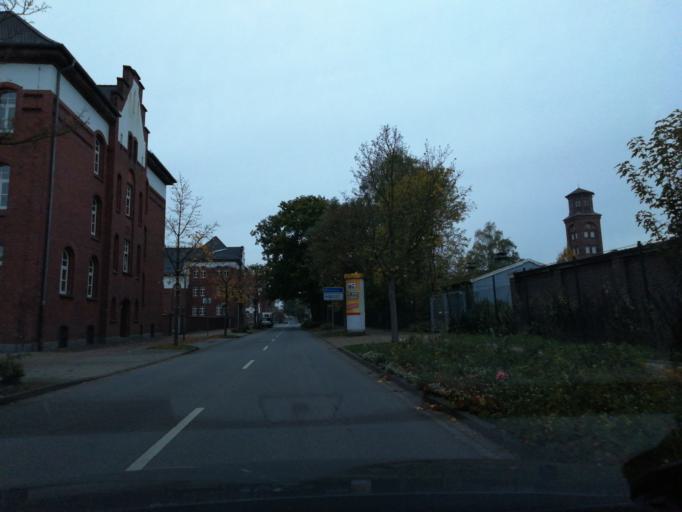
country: DE
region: Lower Saxony
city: Wilhelmshaven
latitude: 53.5176
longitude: 8.1265
